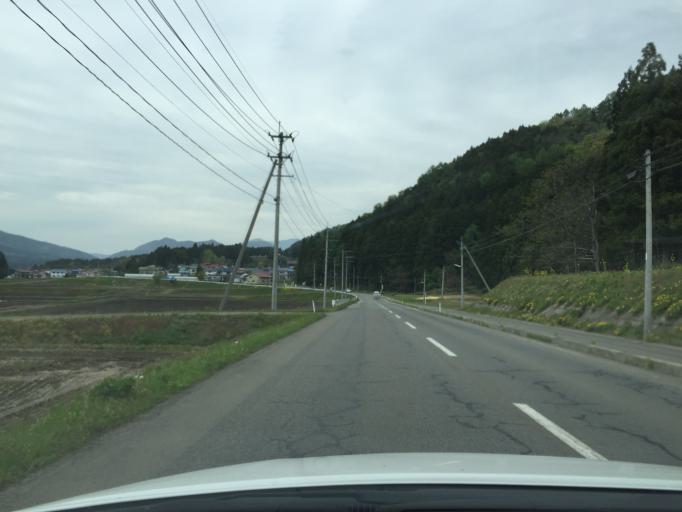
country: JP
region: Fukushima
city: Inawashiro
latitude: 37.5514
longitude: 140.1404
